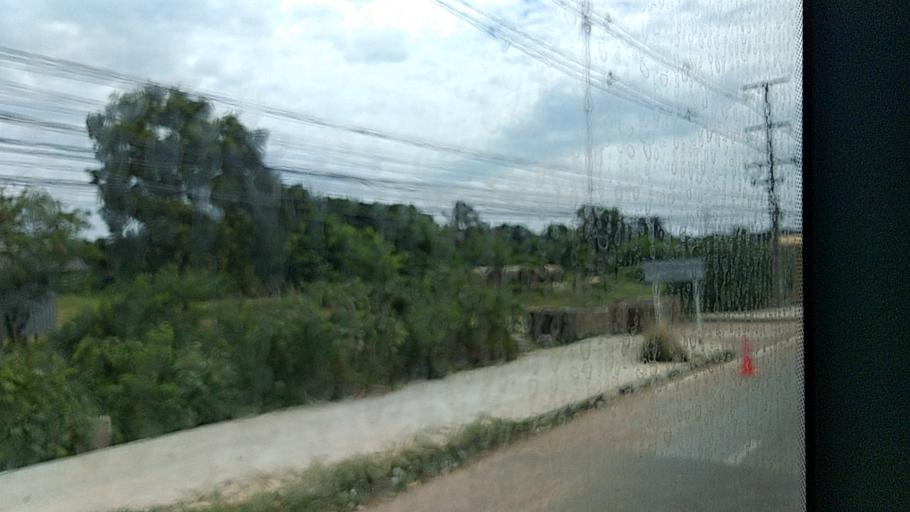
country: TH
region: Maha Sarakham
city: Maha Sarakham
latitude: 16.2358
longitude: 103.2707
